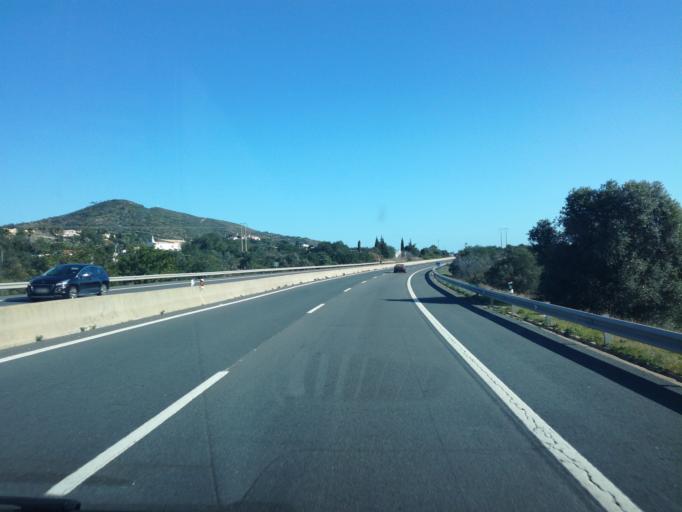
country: PT
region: Faro
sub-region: Faro
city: Santa Barbara de Nexe
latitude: 37.0962
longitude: -7.9552
